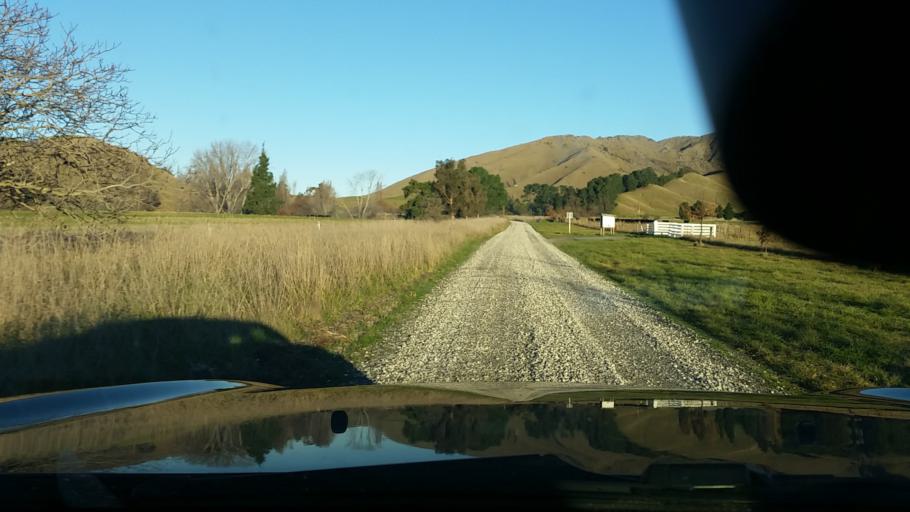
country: NZ
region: Marlborough
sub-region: Marlborough District
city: Blenheim
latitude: -41.7334
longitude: 174.0381
